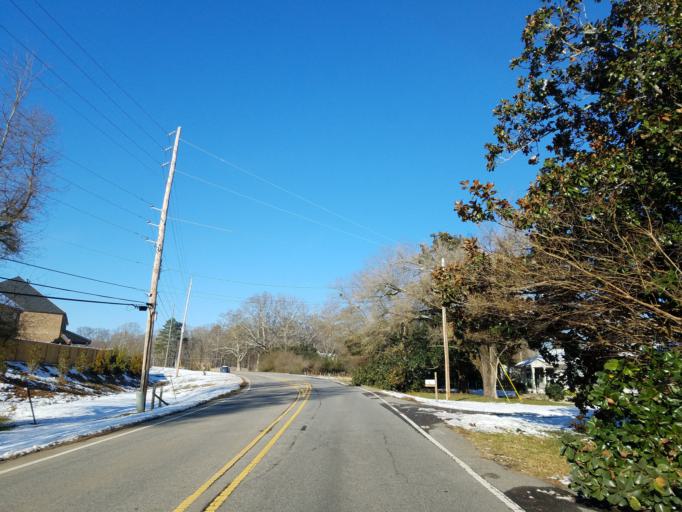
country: US
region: Georgia
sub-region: Forsyth County
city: Cumming
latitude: 34.2985
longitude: -84.0998
